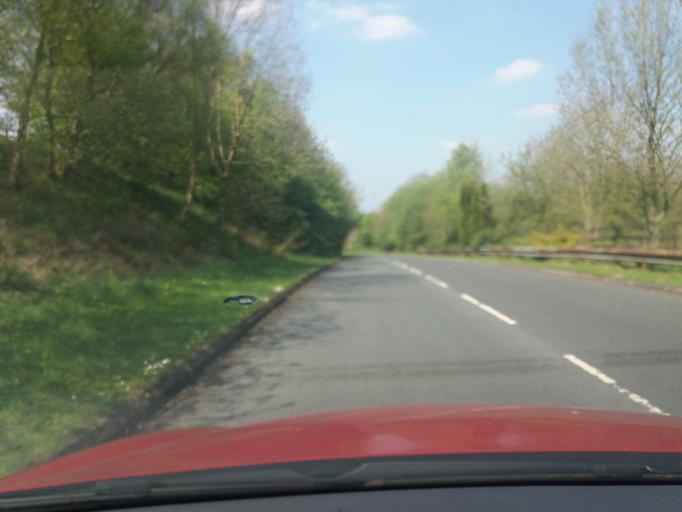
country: GB
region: England
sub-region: Lancashire
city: Clayton-le-Woods
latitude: 53.6948
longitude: -2.6276
